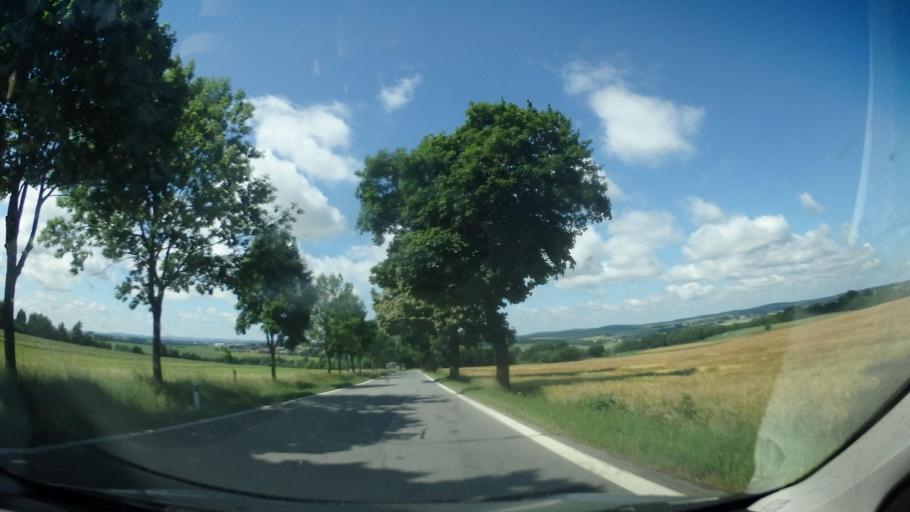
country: CZ
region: Vysocina
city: Zd'ar nad Sazavou Druhy
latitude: 49.5936
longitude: 15.9838
